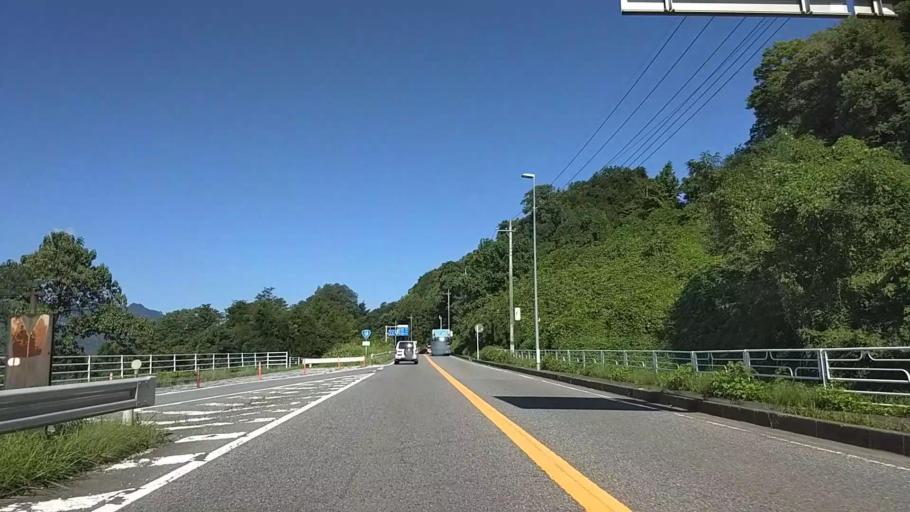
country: JP
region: Gunma
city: Annaka
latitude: 36.3160
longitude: 138.8036
